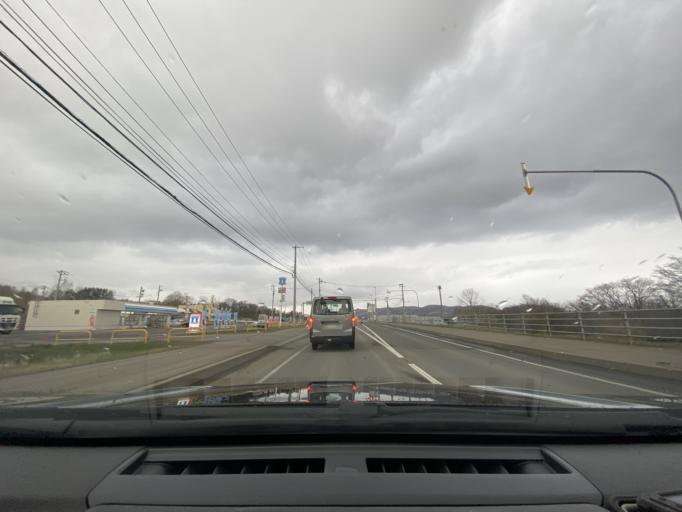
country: JP
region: Hokkaido
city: Otofuke
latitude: 43.2311
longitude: 143.5459
